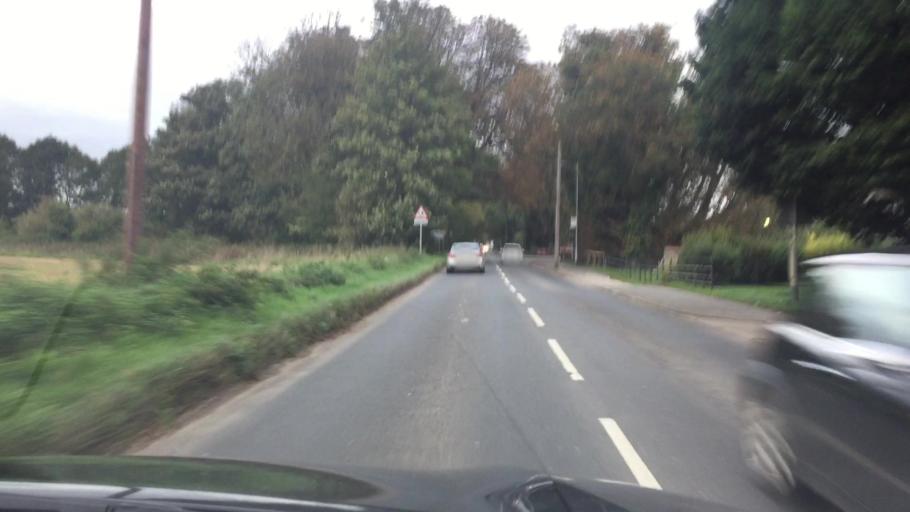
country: GB
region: England
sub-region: East Riding of Yorkshire
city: Pocklington
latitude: 53.9253
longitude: -0.7847
